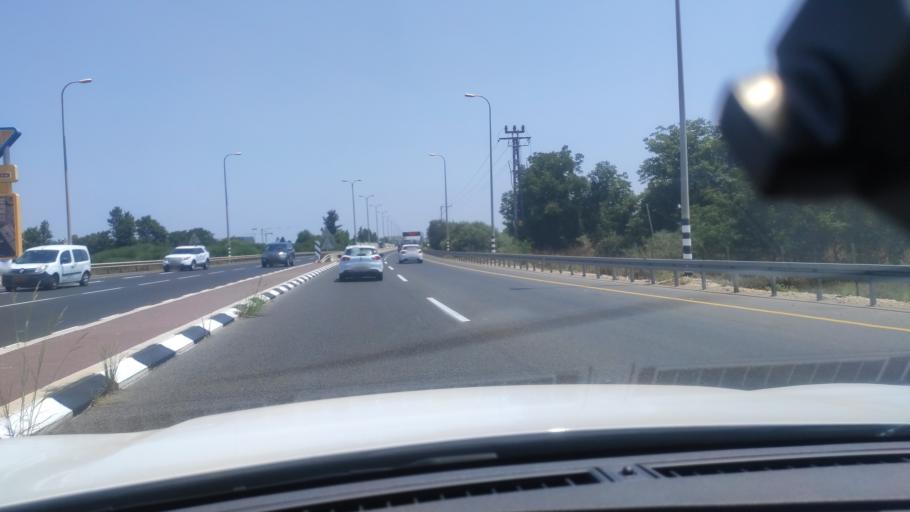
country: IL
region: Central District
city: Kfar Saba
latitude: 32.1523
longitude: 34.9217
